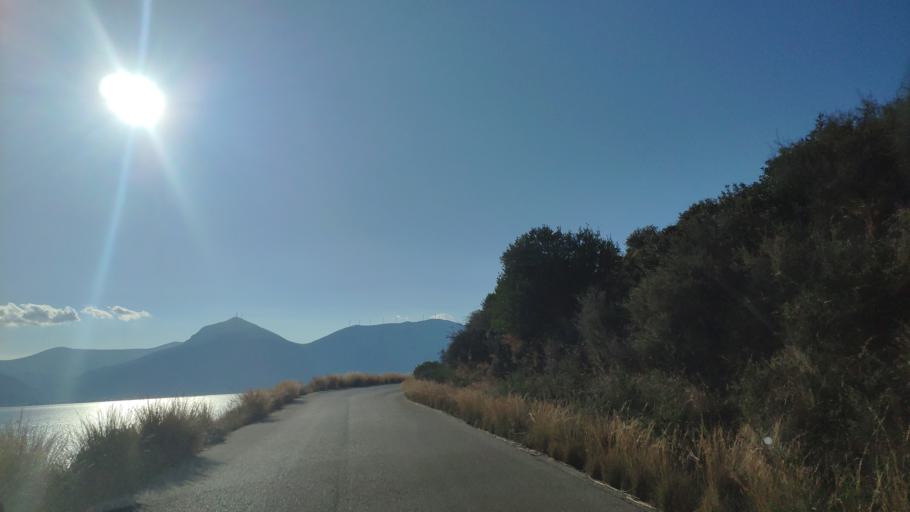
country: GR
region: Attica
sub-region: Nomos Piraios
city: Megalochori
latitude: 37.5813
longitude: 23.3489
